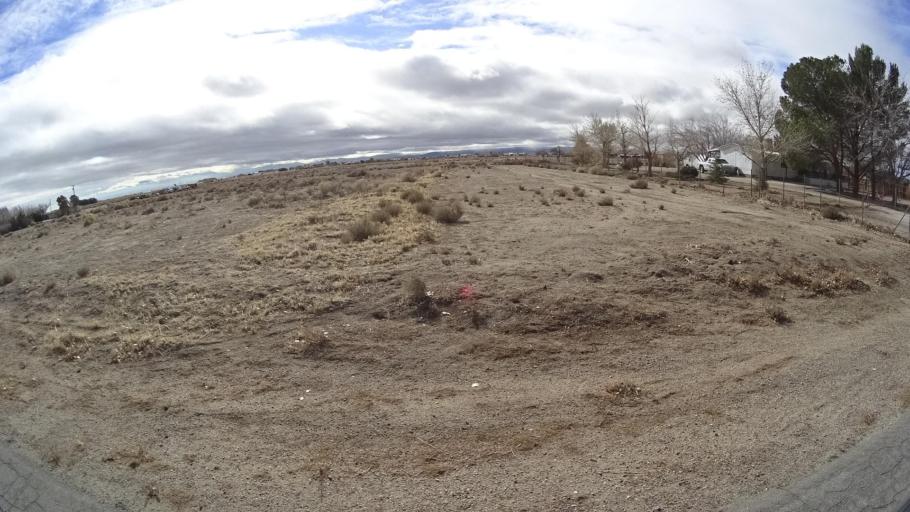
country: US
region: California
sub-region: Kern County
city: Rosamond
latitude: 34.8346
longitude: -118.2526
